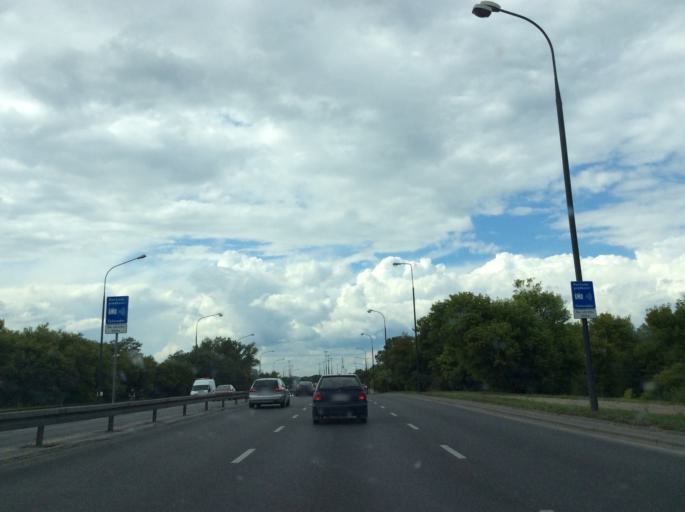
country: PL
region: Masovian Voivodeship
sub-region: Warszawa
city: Bialoleka
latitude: 52.3003
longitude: 20.9927
